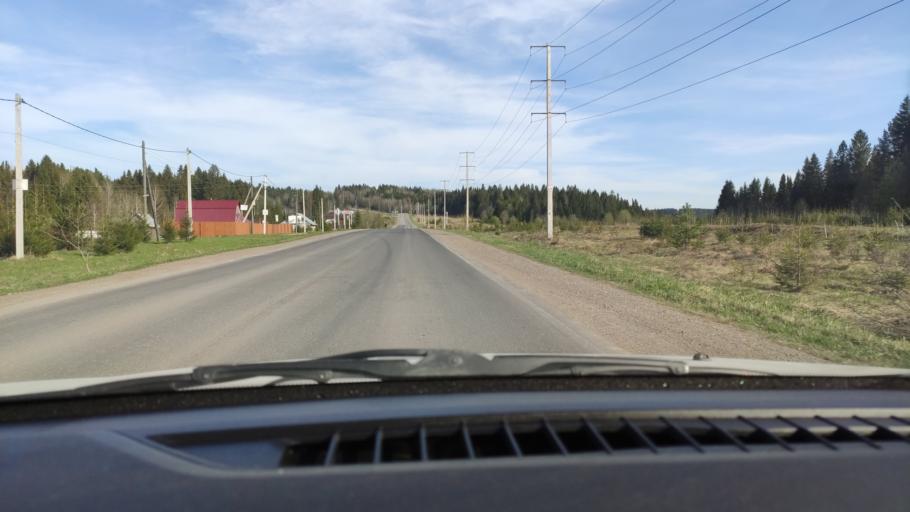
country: RU
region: Perm
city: Novyye Lyady
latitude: 57.9348
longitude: 56.6331
